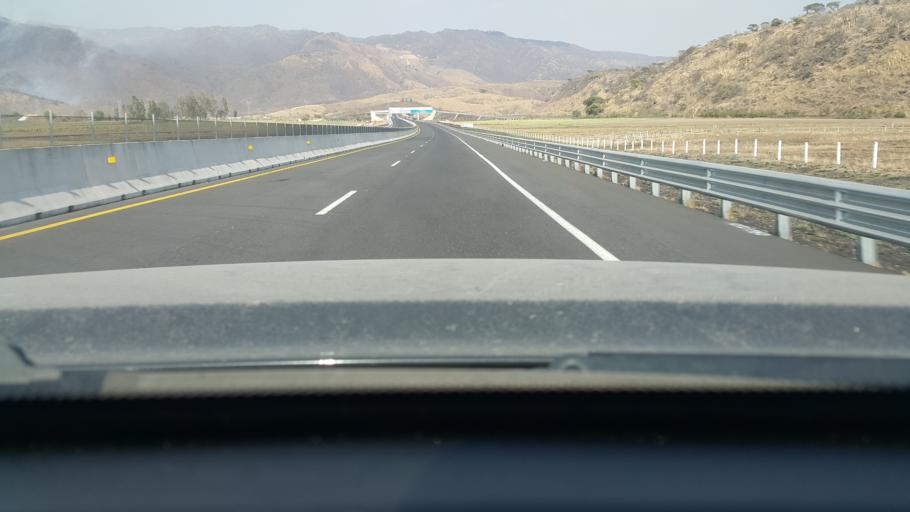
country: MX
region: Nayarit
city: Jala
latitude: 21.0772
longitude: -104.4389
